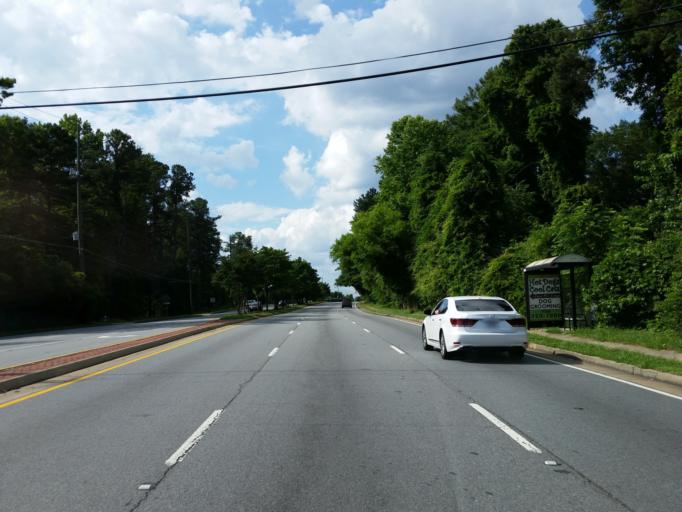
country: US
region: Georgia
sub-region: Fulton County
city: Sandy Springs
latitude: 33.9522
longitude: -84.4114
